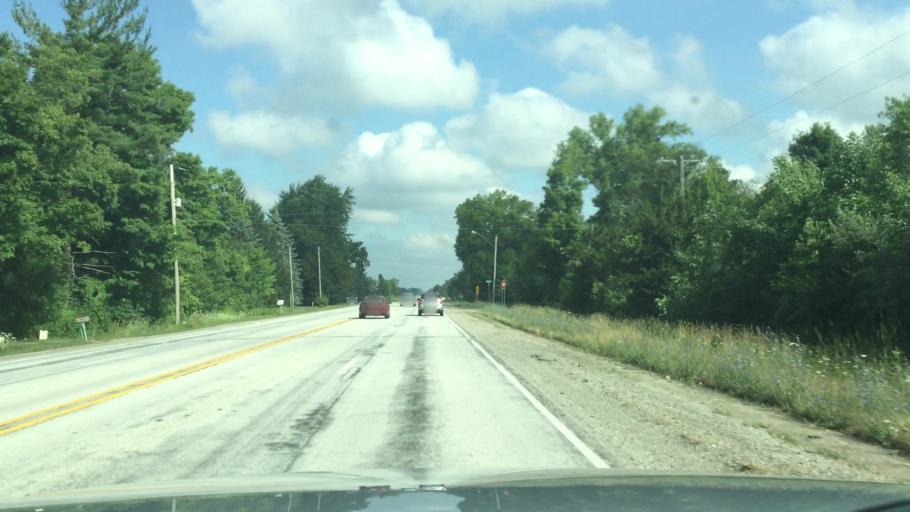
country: US
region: Michigan
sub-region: Saginaw County
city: Birch Run
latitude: 43.2278
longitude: -83.7524
